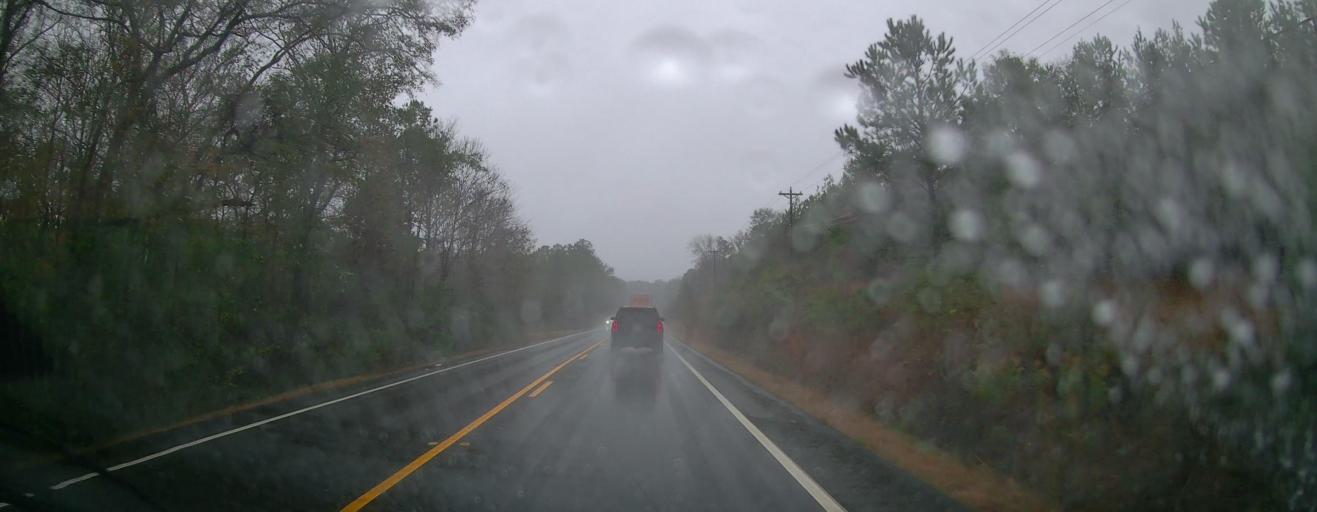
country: US
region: Georgia
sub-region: Putnam County
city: Eatonton
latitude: 33.2294
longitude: -83.4325
